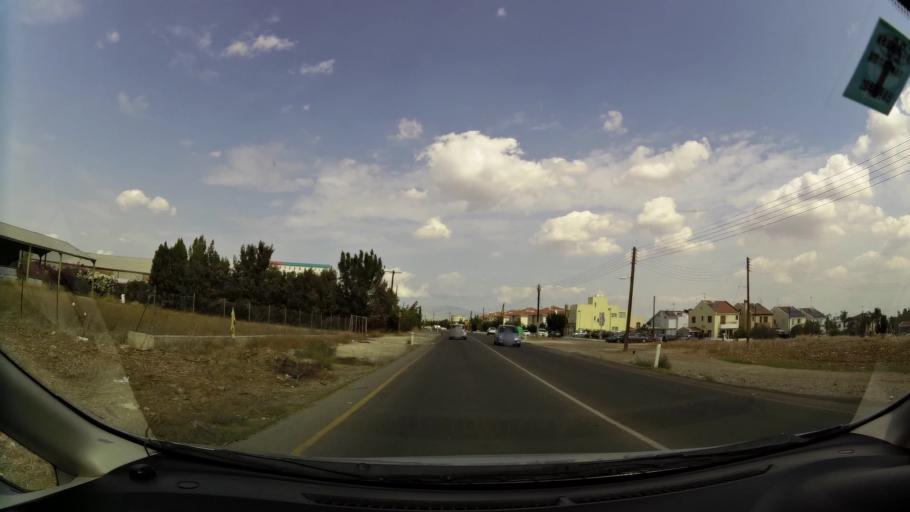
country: CY
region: Lefkosia
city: Tseri
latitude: 35.1086
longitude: 33.3314
